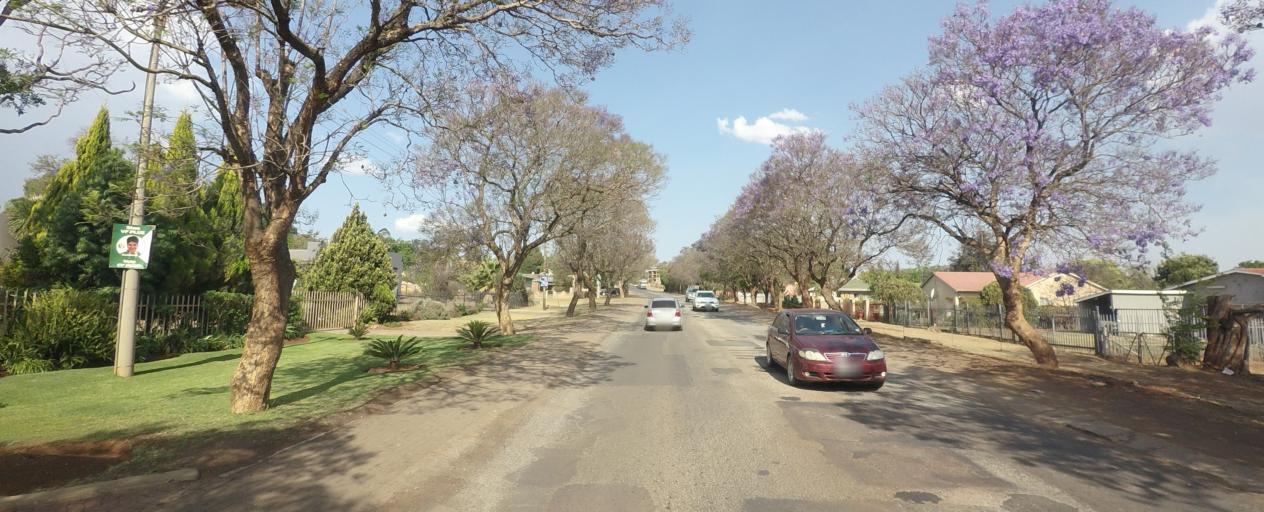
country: ZA
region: Mpumalanga
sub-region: Ehlanzeni District
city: Lydenburg
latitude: -25.1021
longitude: 30.4723
